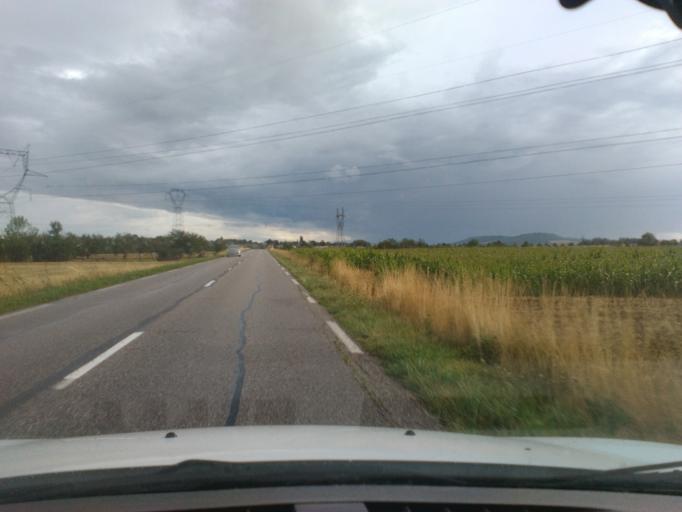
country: FR
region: Lorraine
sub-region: Departement de Meurthe-et-Moselle
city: Vezelise
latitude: 48.4806
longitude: 6.1419
